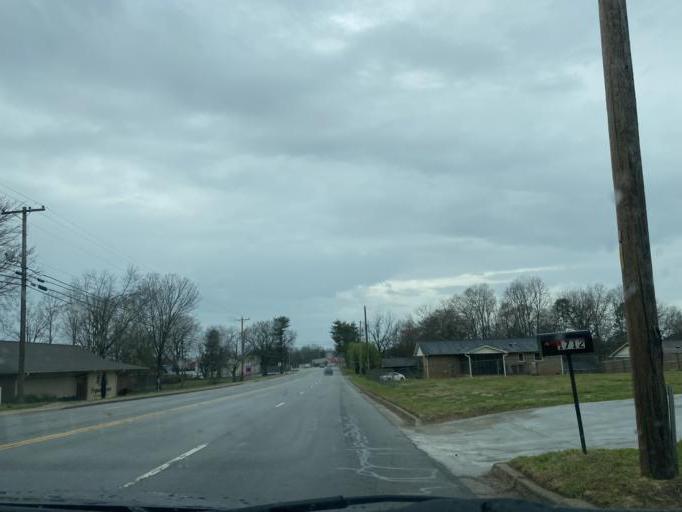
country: US
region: South Carolina
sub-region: Cherokee County
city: Gaffney
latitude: 35.0604
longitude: -81.6739
